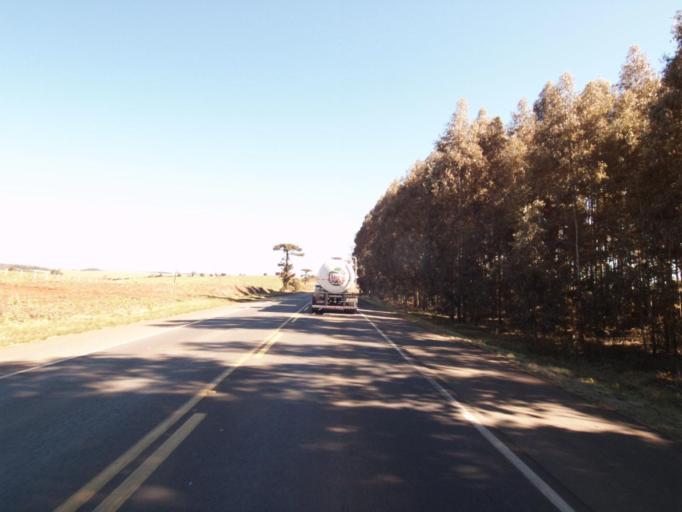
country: BR
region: Santa Catarina
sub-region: Xanxere
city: Xanxere
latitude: -26.8767
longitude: -52.3308
